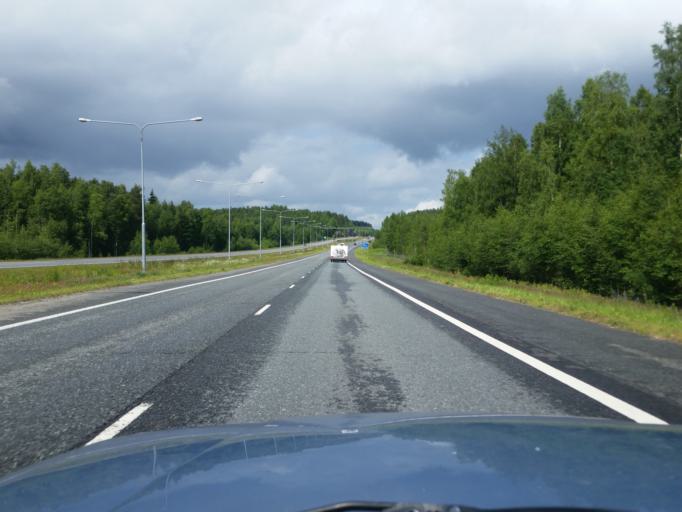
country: FI
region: Paijanne Tavastia
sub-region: Lahti
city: Heinola
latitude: 61.2446
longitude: 26.0508
